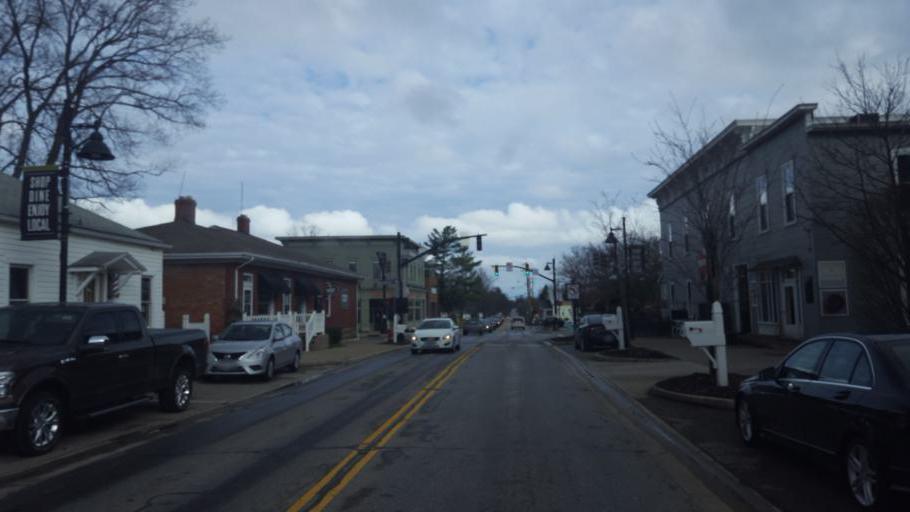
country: US
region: Ohio
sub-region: Delaware County
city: Powell
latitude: 40.1580
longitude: -83.0759
